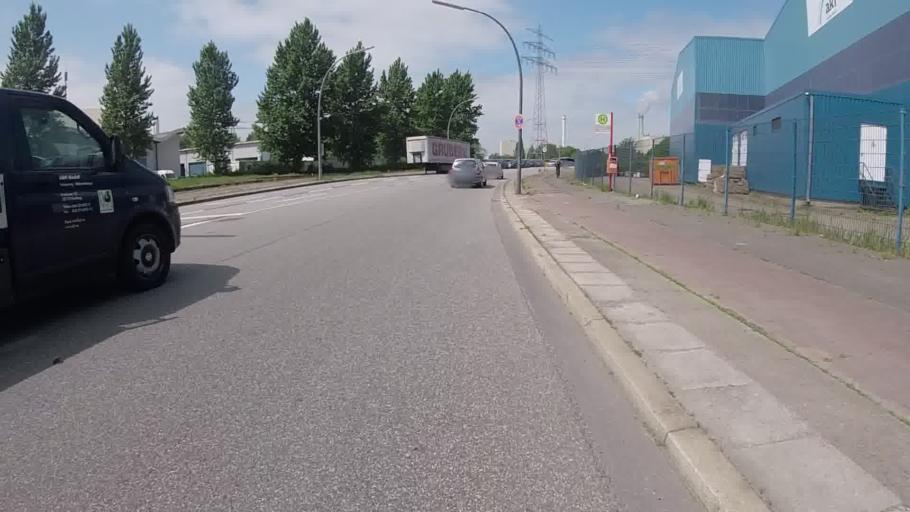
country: DE
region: Hamburg
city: Rothenburgsort
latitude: 53.5275
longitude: 10.0790
